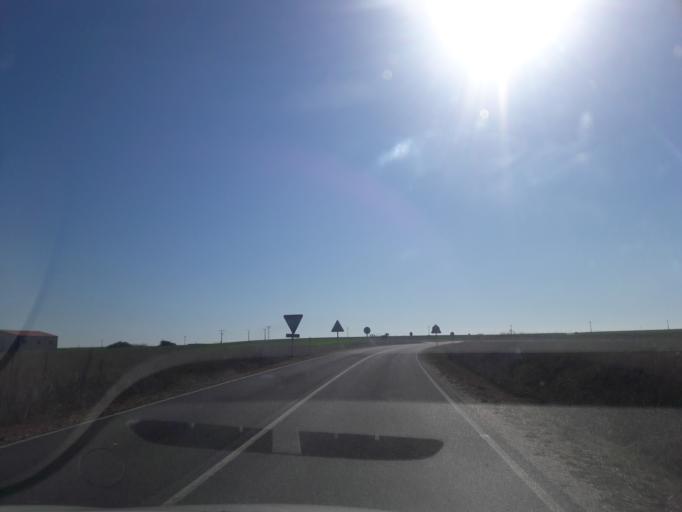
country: ES
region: Castille and Leon
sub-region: Provincia de Salamanca
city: Macotera
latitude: 40.8282
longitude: -5.2788
